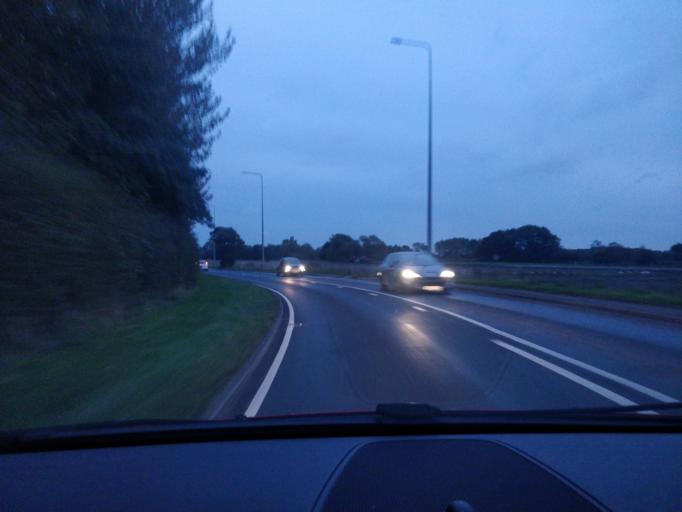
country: GB
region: England
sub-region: Lancashire
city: Ormskirk
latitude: 53.5870
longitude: -2.9138
